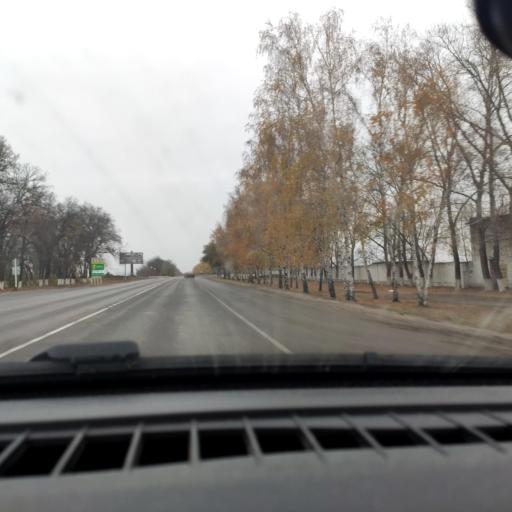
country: RU
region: Voronezj
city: Ostrogozhsk
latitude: 50.8809
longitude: 39.0714
